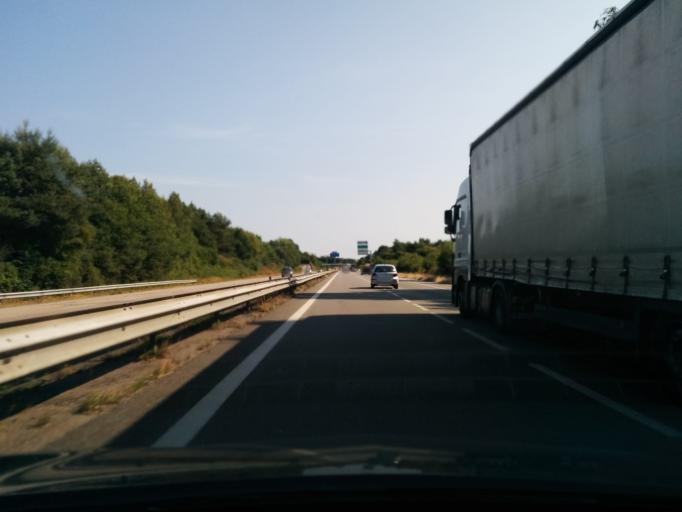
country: FR
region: Limousin
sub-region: Departement de la Haute-Vienne
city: Rilhac-Rancon
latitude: 45.8995
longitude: 1.2921
